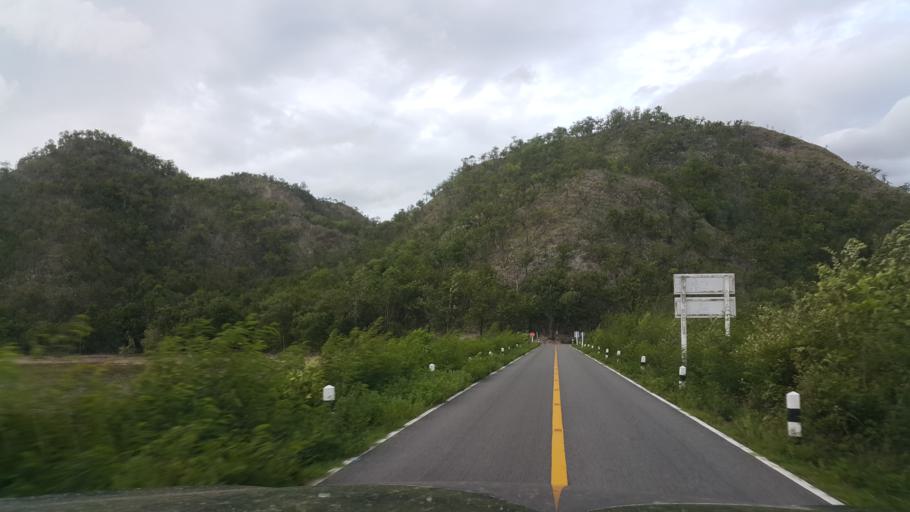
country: TH
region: Sukhothai
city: Thung Saliam
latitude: 17.1791
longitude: 99.4824
